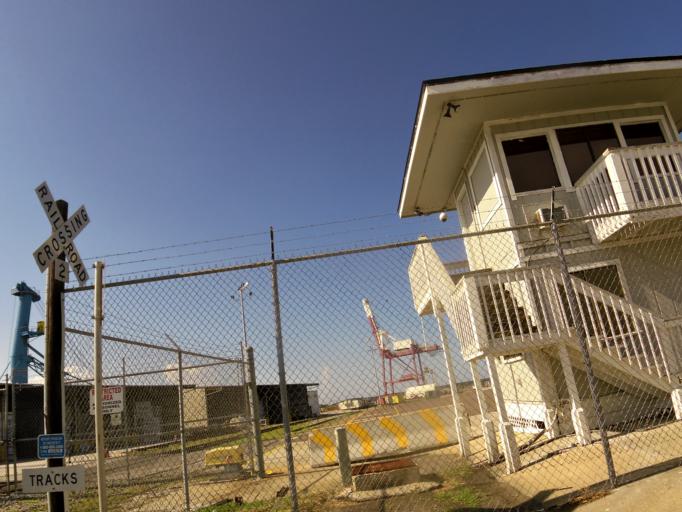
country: US
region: Florida
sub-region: Nassau County
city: Fernandina Beach
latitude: 30.6765
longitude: -81.4639
